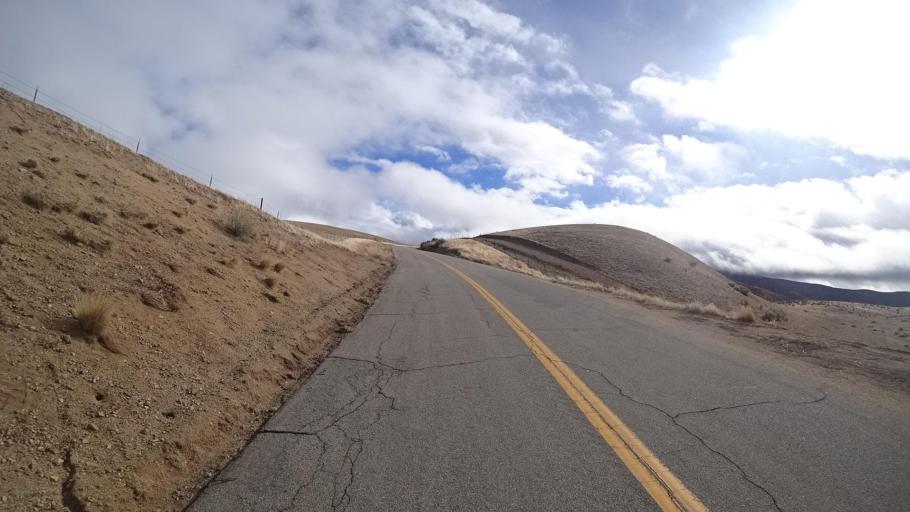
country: US
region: California
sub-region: Kern County
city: Maricopa
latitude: 34.9023
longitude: -119.3725
